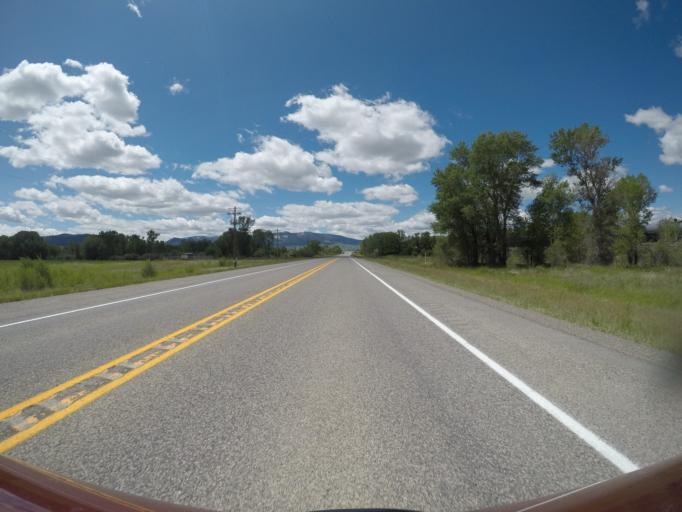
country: US
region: Montana
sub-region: Park County
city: Livingston
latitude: 45.6782
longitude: -110.5283
